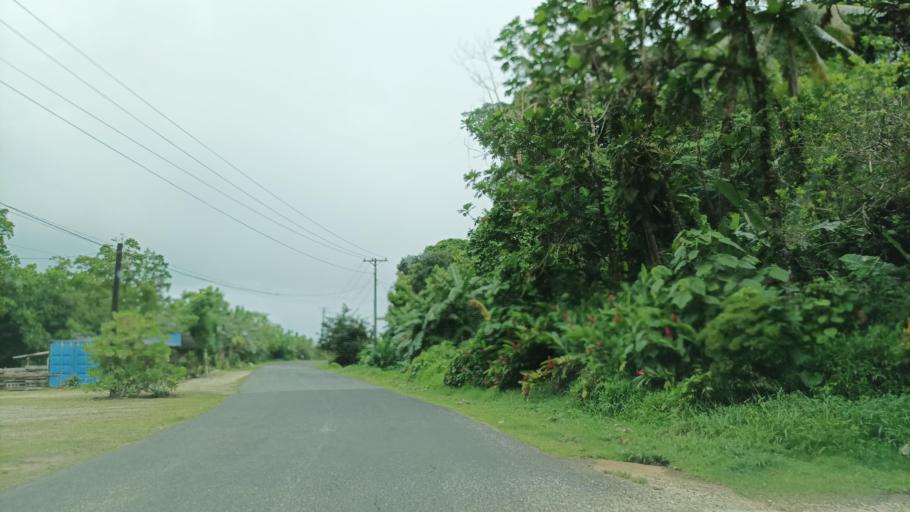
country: FM
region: Pohnpei
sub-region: Kolonia Municipality
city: Kolonia
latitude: 6.9587
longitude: 158.2492
